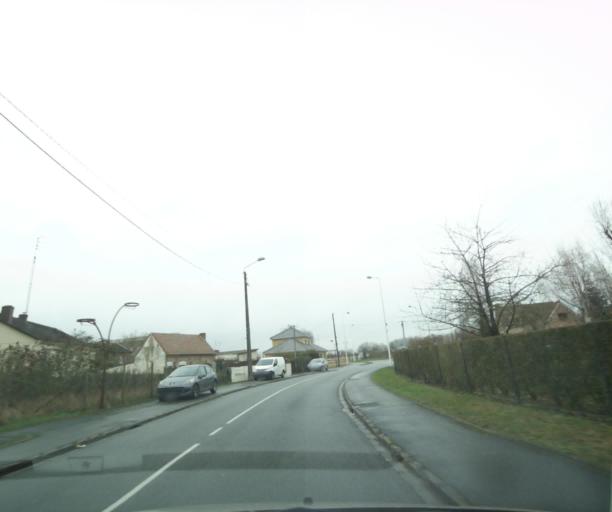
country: FR
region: Nord-Pas-de-Calais
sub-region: Departement du Nord
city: Haulchin
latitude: 50.3244
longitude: 3.4385
